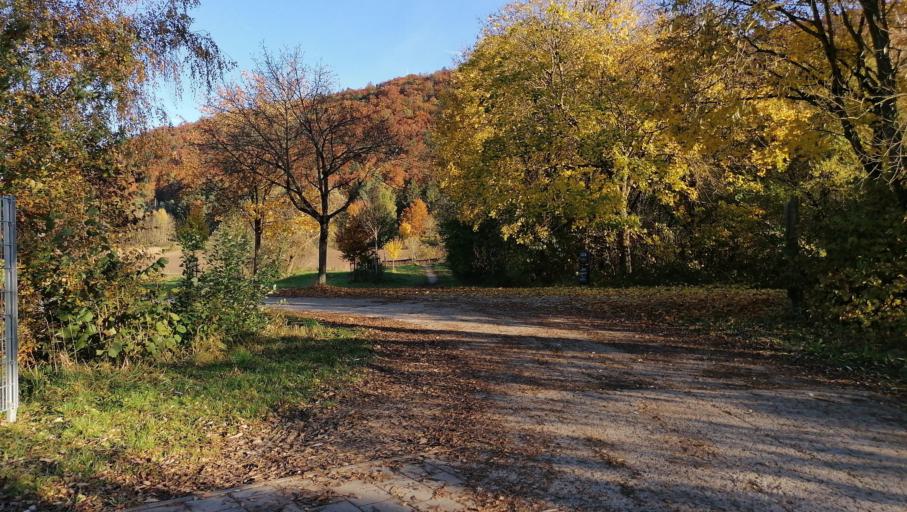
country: DE
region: Bavaria
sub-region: Upper Palatinate
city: Dietfurt
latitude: 49.0225
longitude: 11.5664
